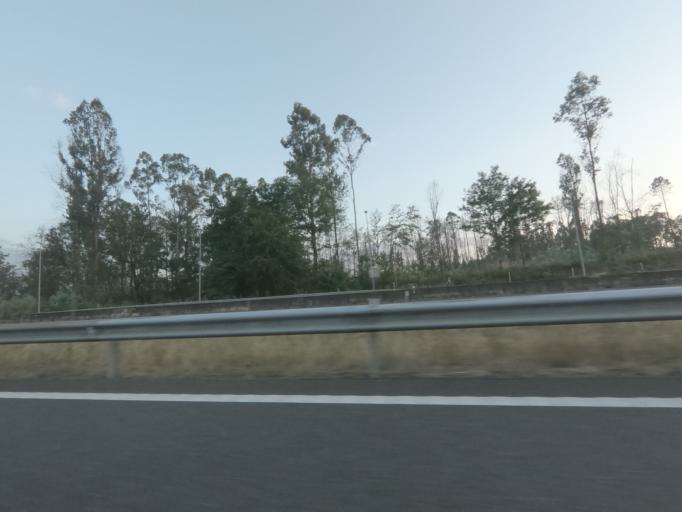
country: ES
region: Galicia
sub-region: Provincia de Pontevedra
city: Ponteareas
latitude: 42.1443
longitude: -8.4740
